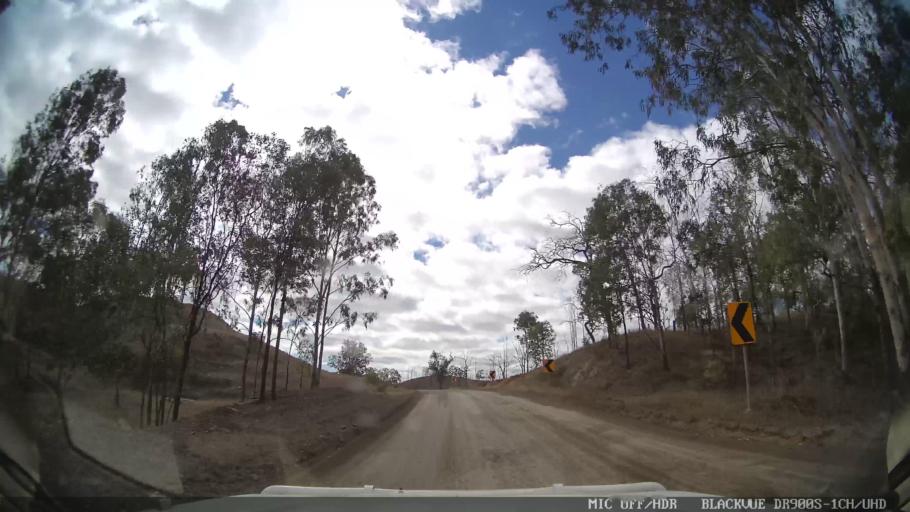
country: AU
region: Queensland
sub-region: Gladstone
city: Toolooa
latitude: -24.6186
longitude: 151.2977
